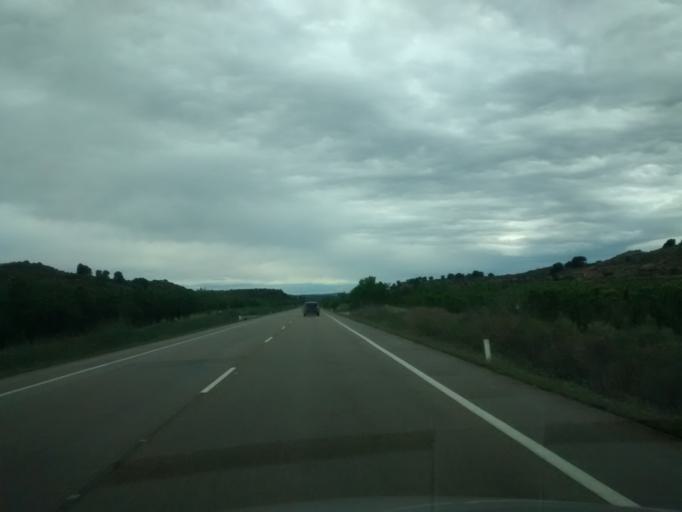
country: ES
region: Aragon
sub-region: Provincia de Zaragoza
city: Maella
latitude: 41.1765
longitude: 0.0582
